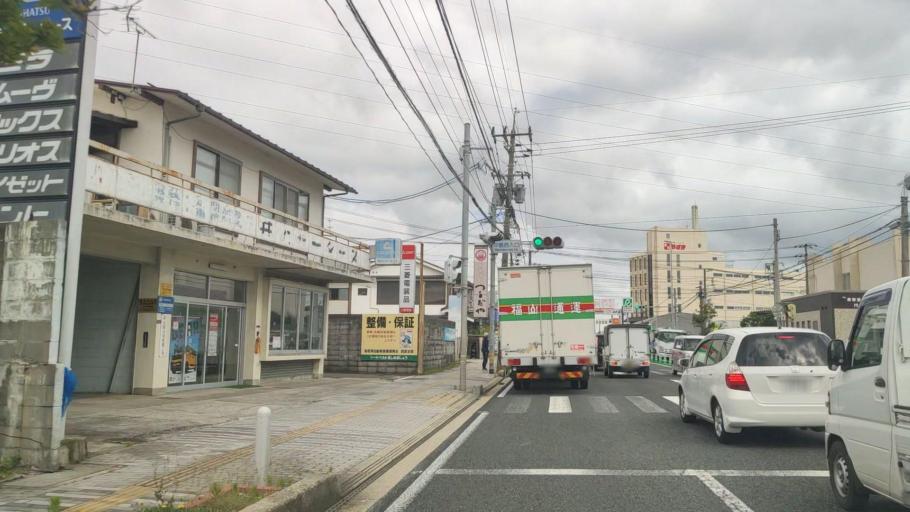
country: JP
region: Tottori
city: Yonago
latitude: 35.4345
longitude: 133.3492
